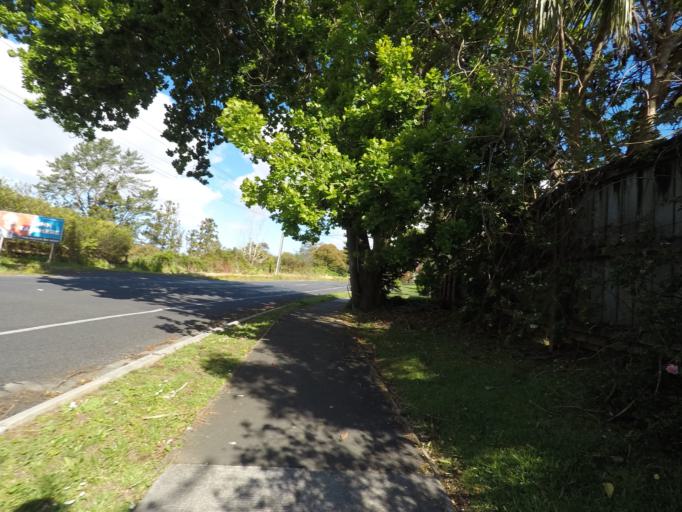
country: NZ
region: Auckland
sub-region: Auckland
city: Rosebank
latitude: -36.8550
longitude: 174.6033
